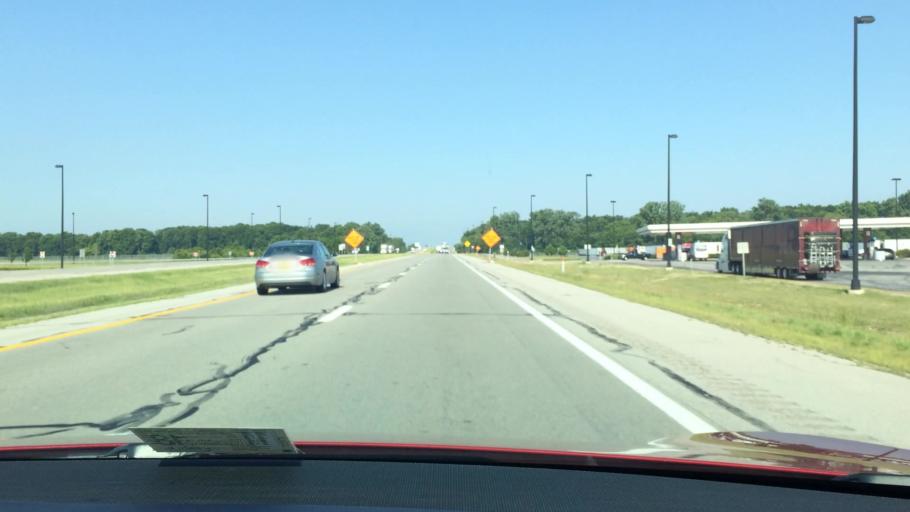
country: US
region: Ohio
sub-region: Williams County
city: West Unity
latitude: 41.6046
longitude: -84.4067
